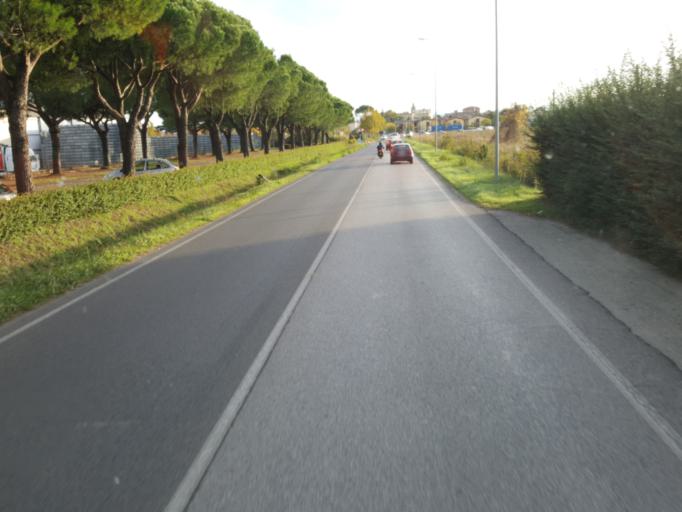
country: IT
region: Emilia-Romagna
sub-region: Provincia di Ravenna
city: Faenza
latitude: 44.3010
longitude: 11.8844
